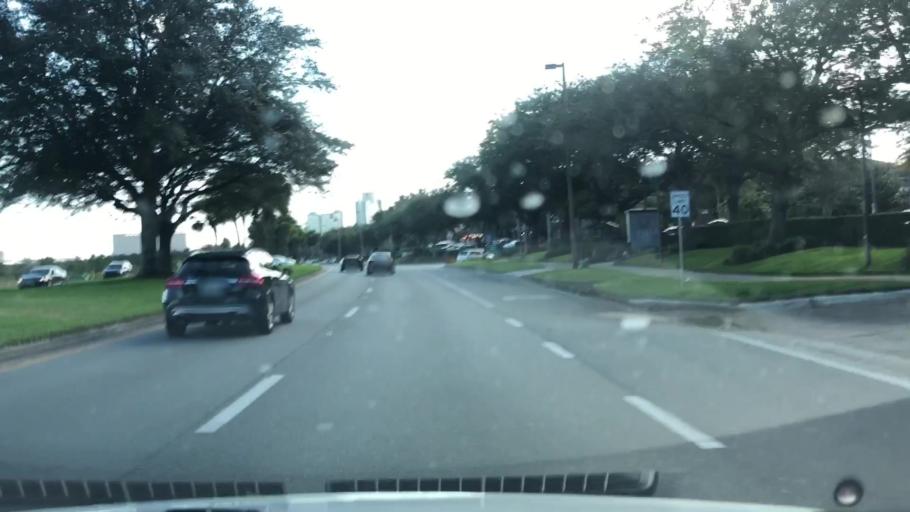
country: US
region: Florida
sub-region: Orange County
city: Doctor Phillips
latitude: 28.4405
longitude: -81.4682
